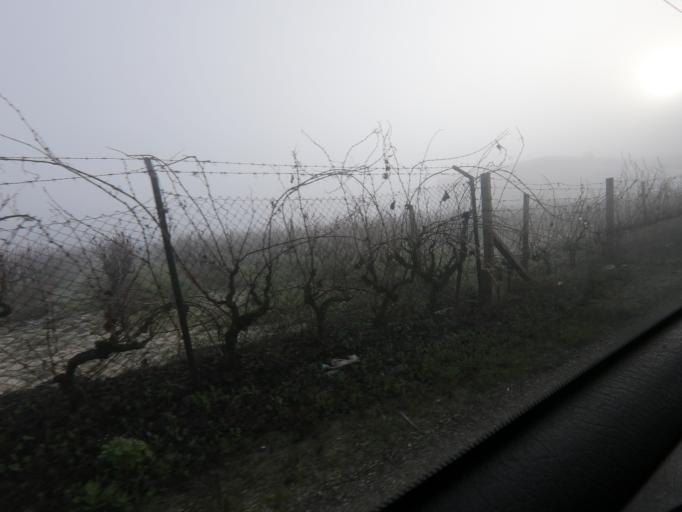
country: PT
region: Setubal
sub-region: Palmela
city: Palmela
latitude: 38.5950
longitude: -8.8421
